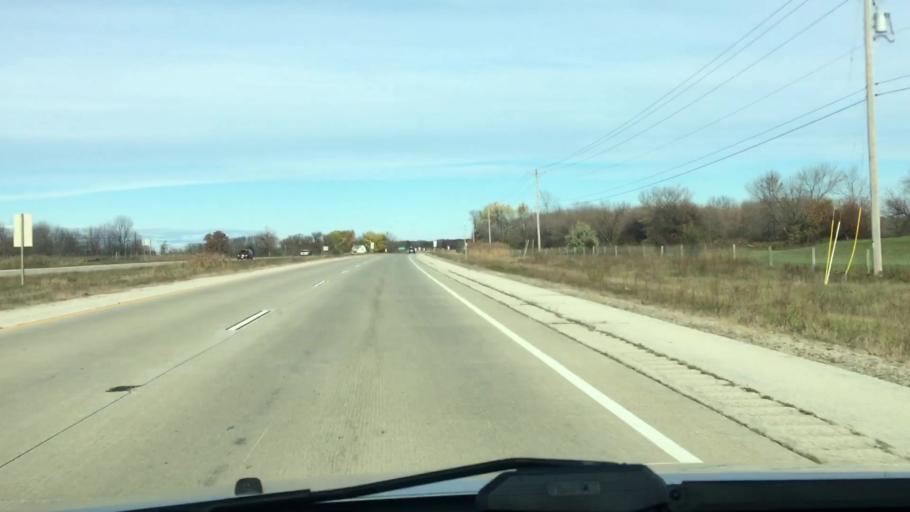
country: US
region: Wisconsin
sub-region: Brown County
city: Bellevue
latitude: 44.5770
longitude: -87.8738
